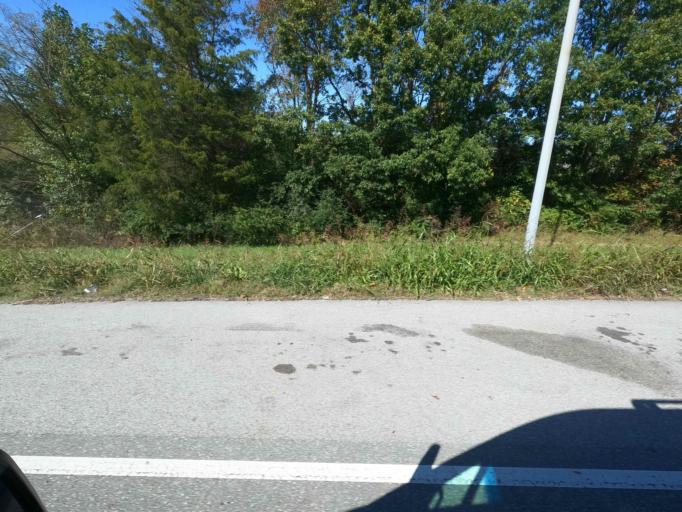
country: US
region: Tennessee
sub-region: Marion County
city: Monteagle
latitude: 35.2323
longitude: -85.8281
